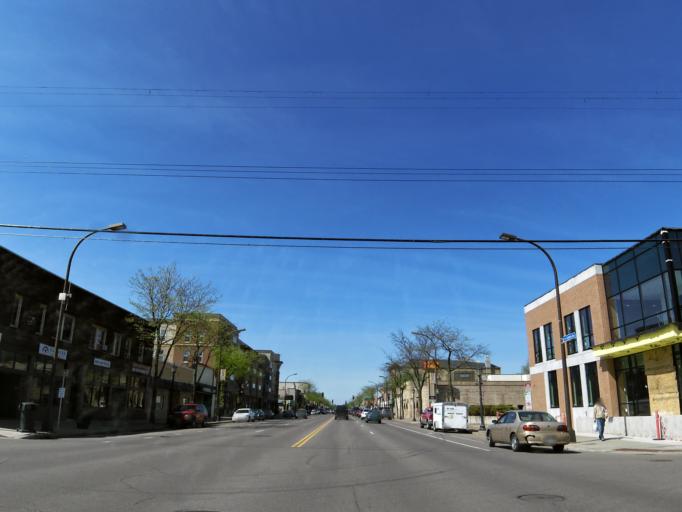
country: US
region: Minnesota
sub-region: Hennepin County
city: Saint Anthony
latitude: 45.0108
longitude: -93.2474
